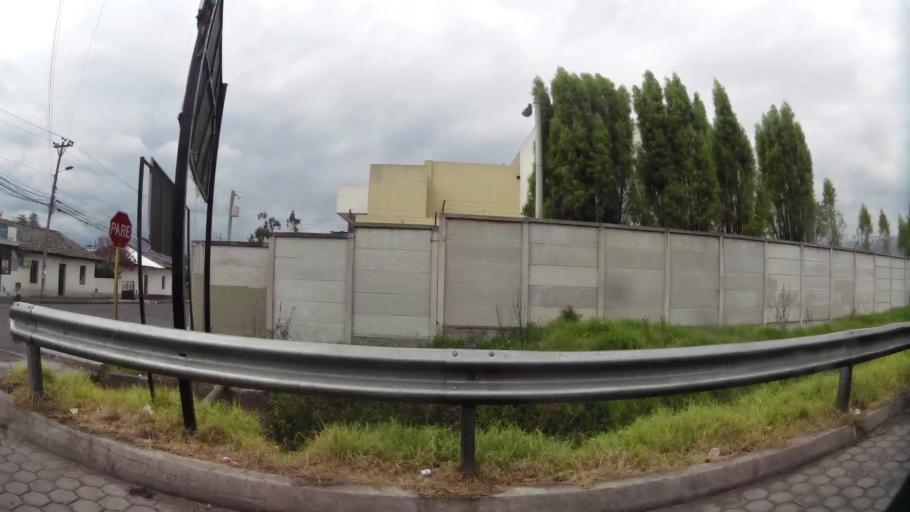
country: EC
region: Pichincha
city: Sangolqui
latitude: -0.3537
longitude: -78.4755
